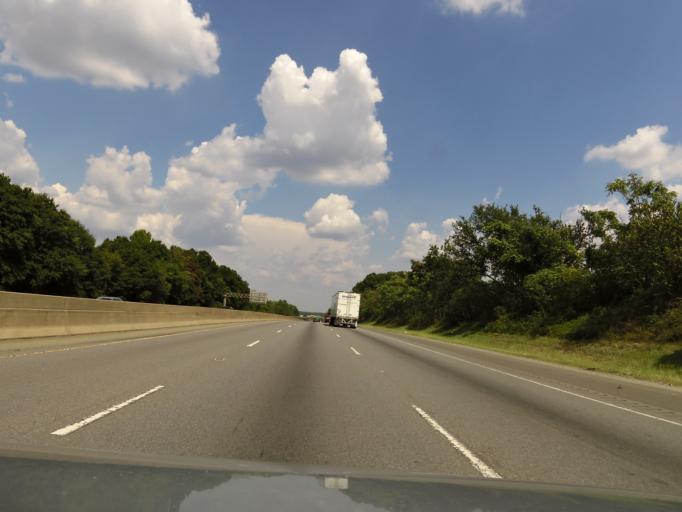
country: US
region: North Carolina
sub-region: Gaston County
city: Gastonia
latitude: 35.2811
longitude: -81.2162
